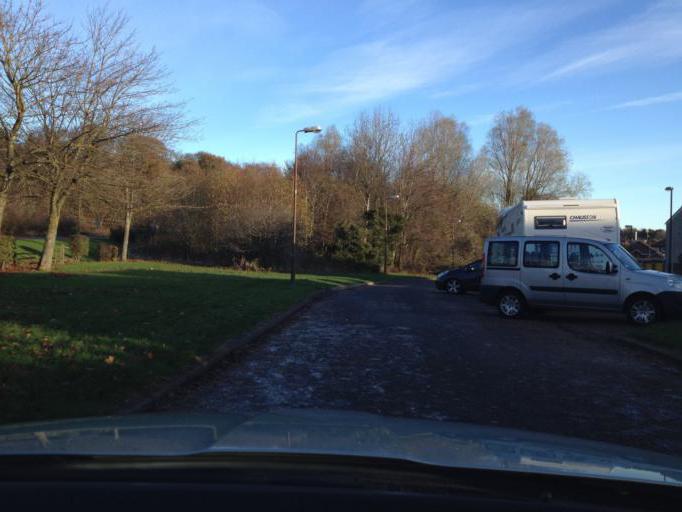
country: GB
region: Scotland
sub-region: West Lothian
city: Livingston
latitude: 55.8978
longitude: -3.5067
